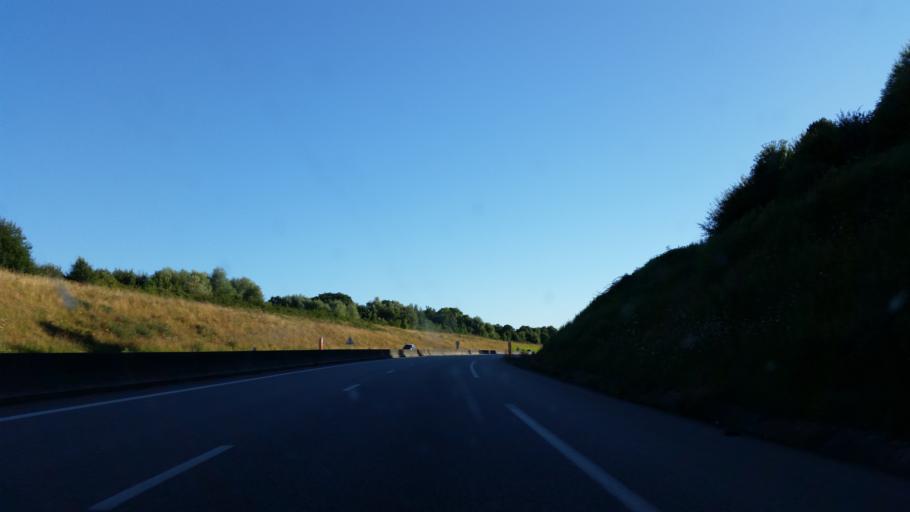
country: FR
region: Lower Normandy
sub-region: Departement du Calvados
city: La Riviere-Saint-Sauveur
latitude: 49.3939
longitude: 0.2614
